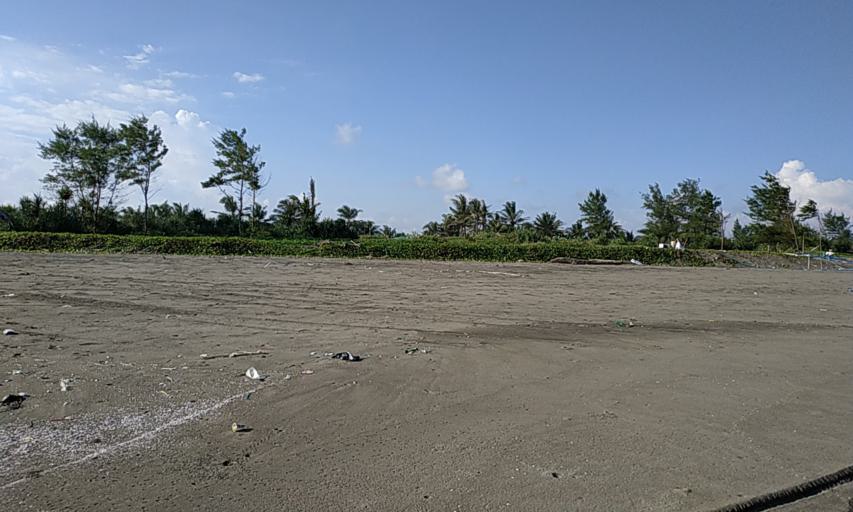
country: ID
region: Central Java
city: Gombong
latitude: -7.7643
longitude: 109.5135
